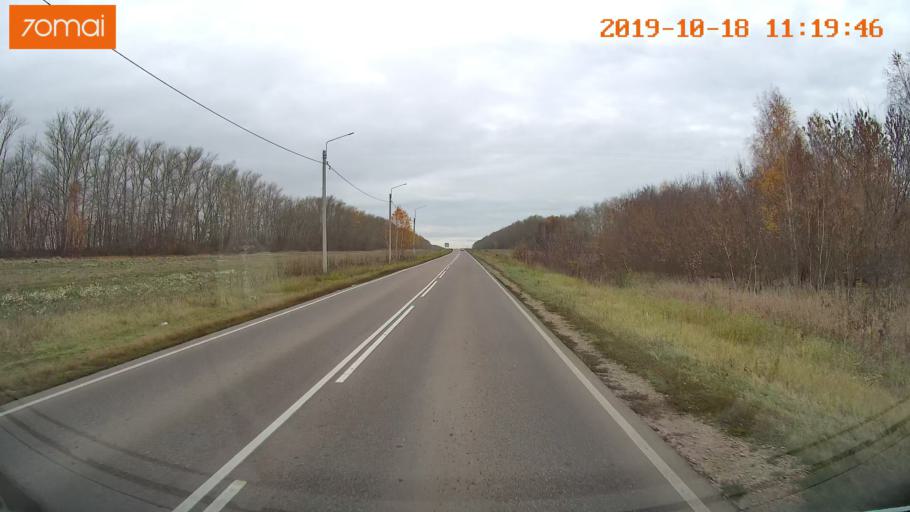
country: RU
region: Tula
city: Kimovsk
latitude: 54.0504
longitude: 38.5554
